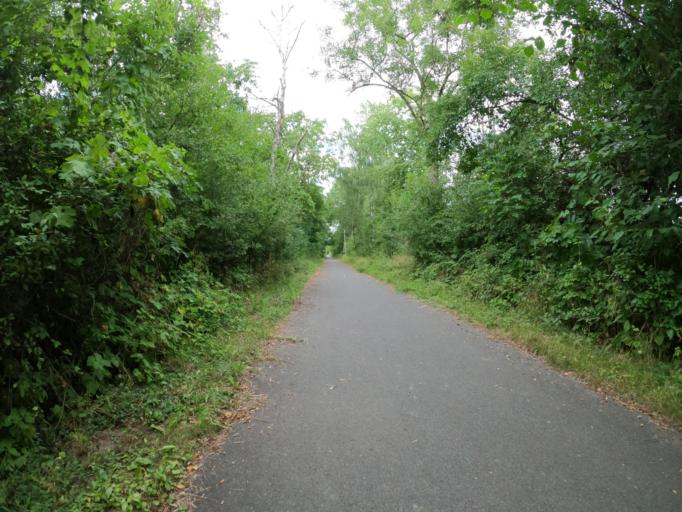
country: DE
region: Mecklenburg-Vorpommern
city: Woldegk
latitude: 53.3630
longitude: 13.5900
